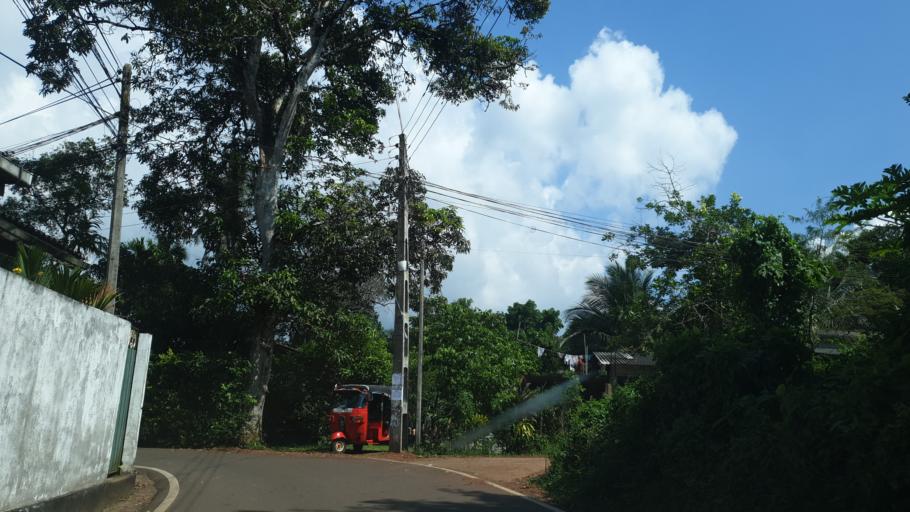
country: LK
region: Western
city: Panadura
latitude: 6.7129
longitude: 79.9615
